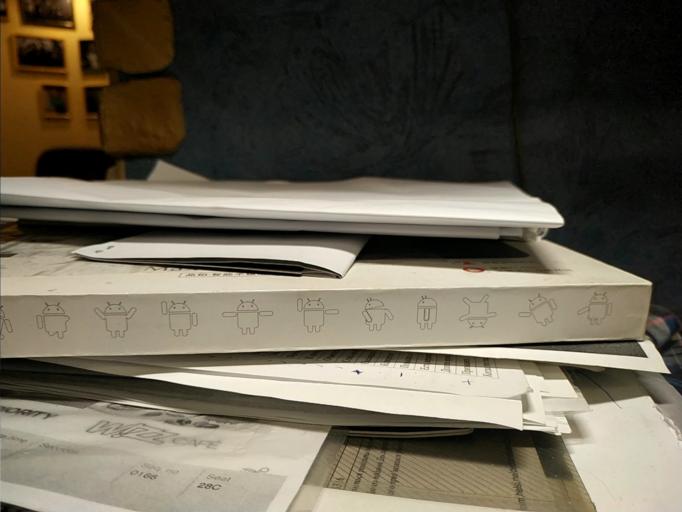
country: RU
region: Tverskaya
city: Zubtsov
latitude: 56.0810
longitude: 34.7980
